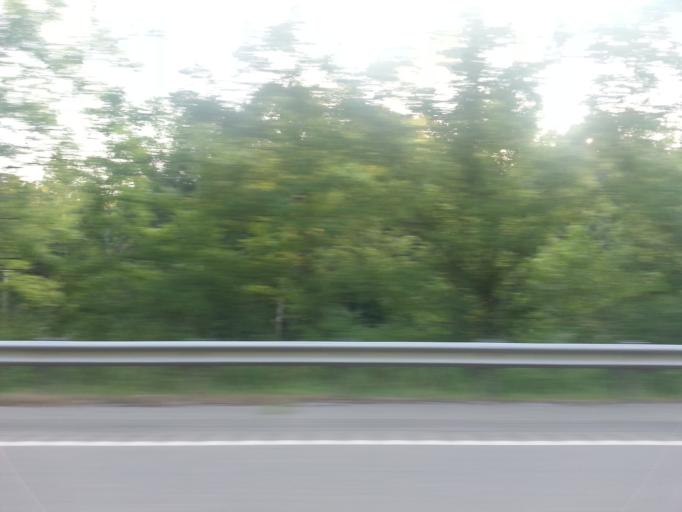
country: US
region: Tennessee
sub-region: McMinn County
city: Athens
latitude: 35.4836
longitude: -84.5951
